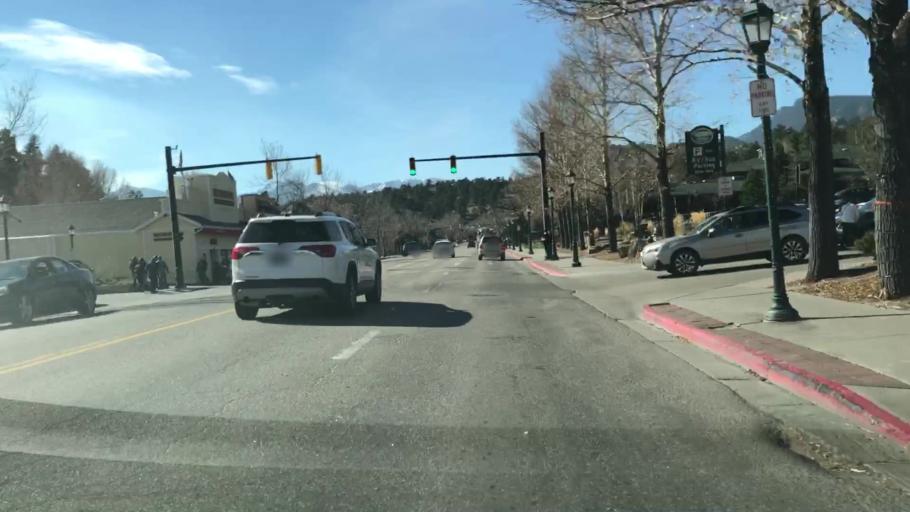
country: US
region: Colorado
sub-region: Larimer County
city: Estes Park
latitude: 40.3774
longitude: -105.5184
